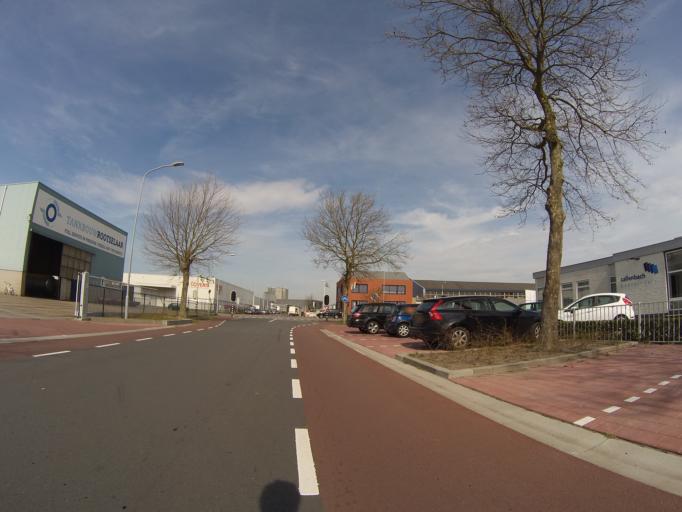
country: NL
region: Gelderland
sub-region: Gemeente Nijkerk
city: Nijkerk
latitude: 52.2322
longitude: 5.4795
